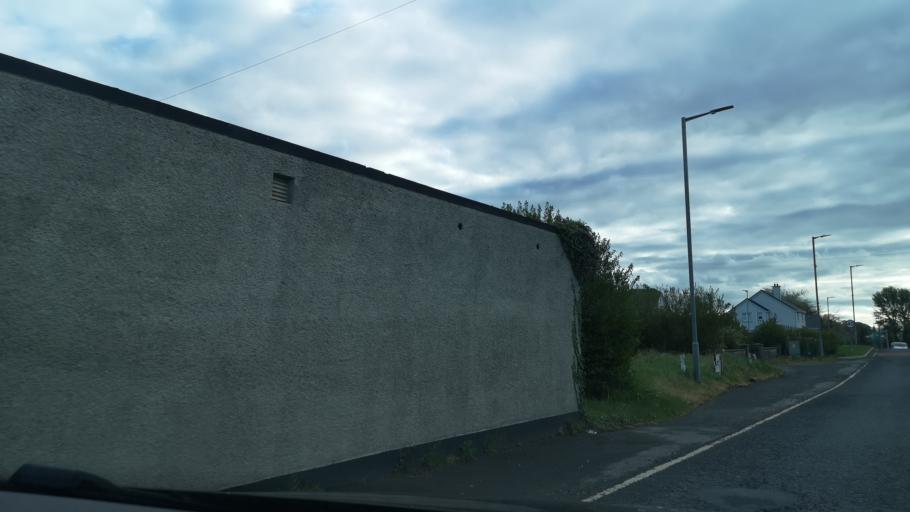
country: GB
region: Northern Ireland
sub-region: Newry and Mourne District
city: Newry
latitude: 54.1832
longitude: -6.3976
